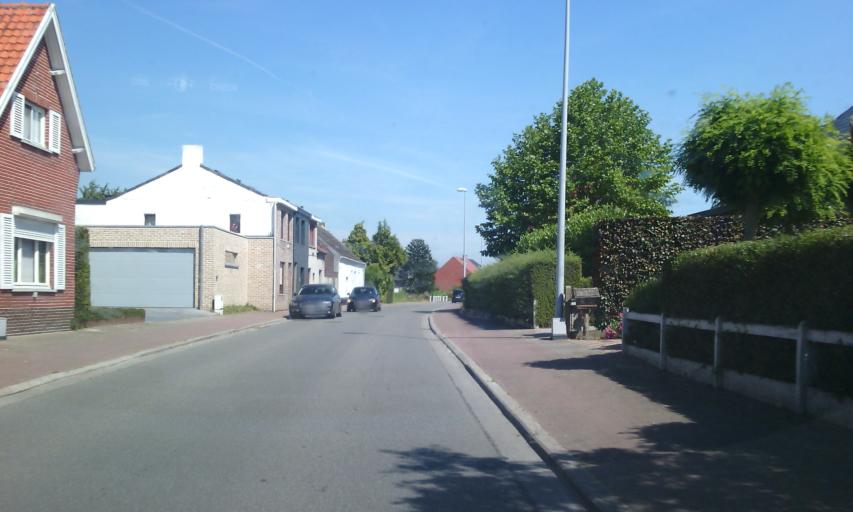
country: BE
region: Flanders
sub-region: Provincie Oost-Vlaanderen
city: Wichelen
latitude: 50.9987
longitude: 3.9913
